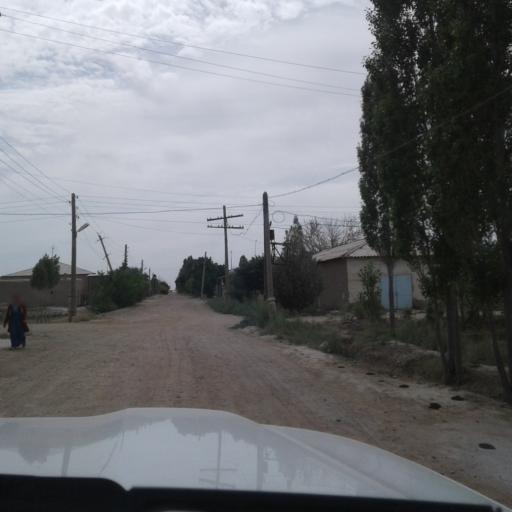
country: TM
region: Dasoguz
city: Tagta
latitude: 41.6000
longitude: 59.8504
